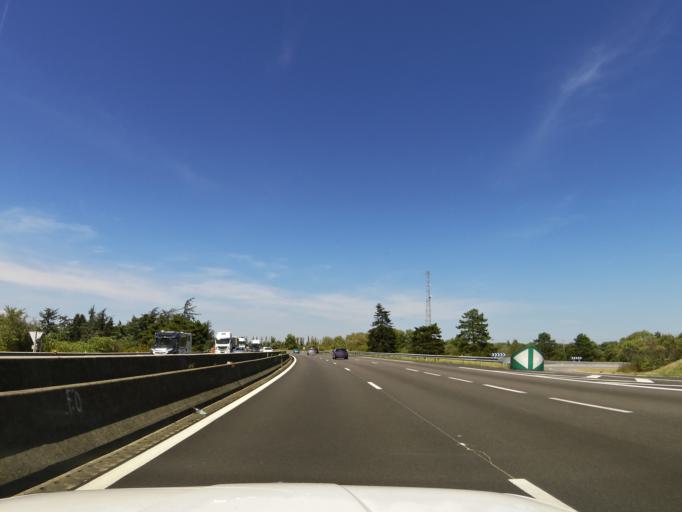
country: FR
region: Rhone-Alpes
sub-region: Departement de la Drome
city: Bourg-les-Valence
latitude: 44.9712
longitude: 4.8859
